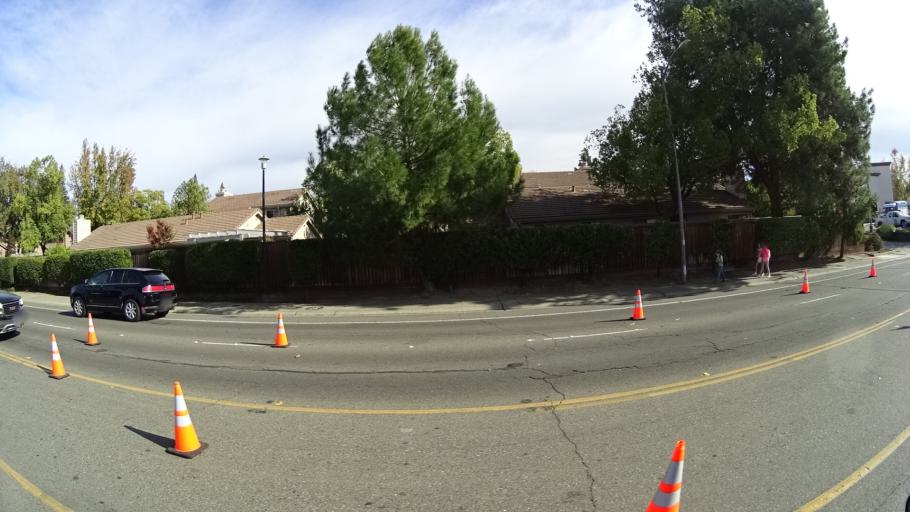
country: US
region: California
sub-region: Sacramento County
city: Fair Oaks
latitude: 38.6654
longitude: -121.2622
